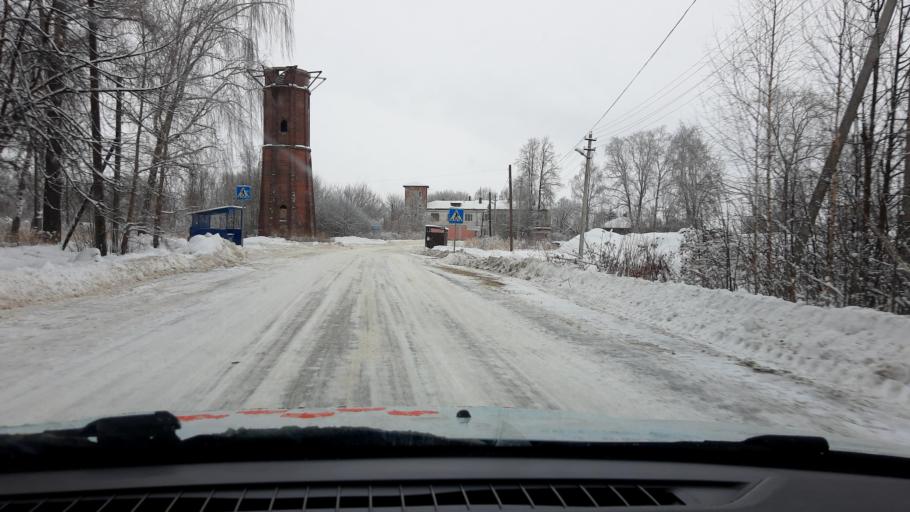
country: RU
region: Nizjnij Novgorod
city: Chkalovsk
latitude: 56.7686
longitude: 43.2596
